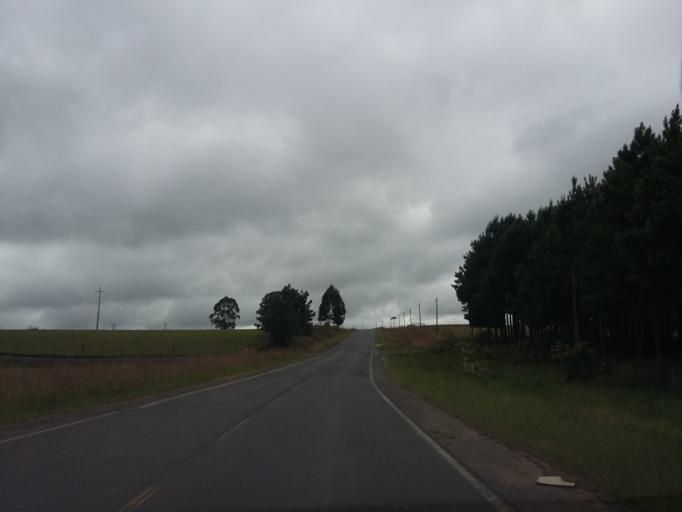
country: BR
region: Santa Catarina
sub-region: Lages
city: Lages
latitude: -27.8154
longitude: -50.2754
